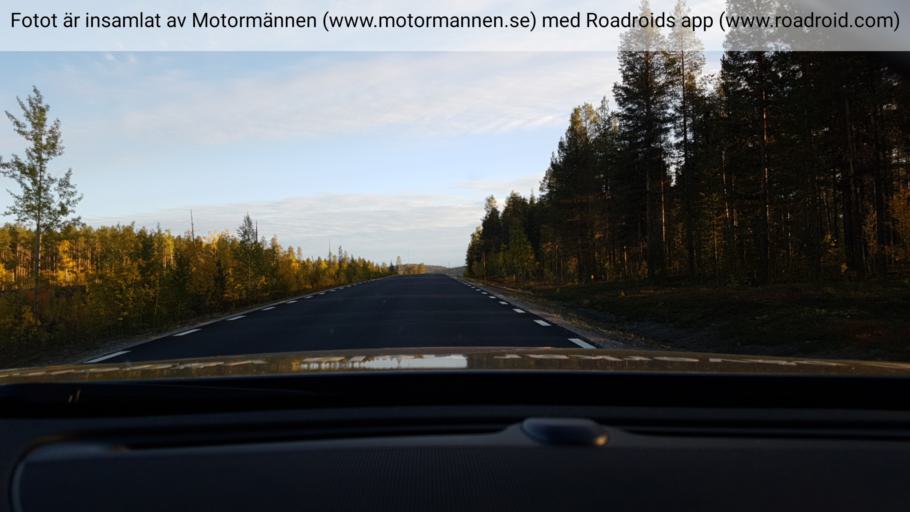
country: SE
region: Norrbotten
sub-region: Jokkmokks Kommun
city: Jokkmokk
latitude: 66.5838
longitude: 19.8056
